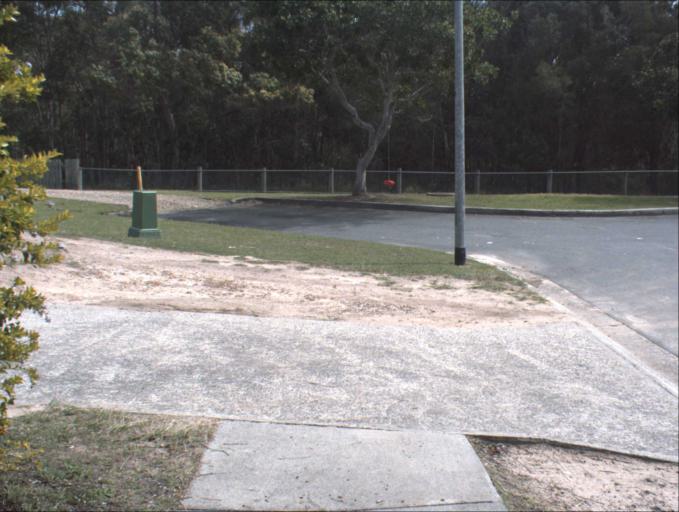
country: AU
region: Queensland
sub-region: Logan
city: Woodridge
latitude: -27.6713
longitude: 153.0808
